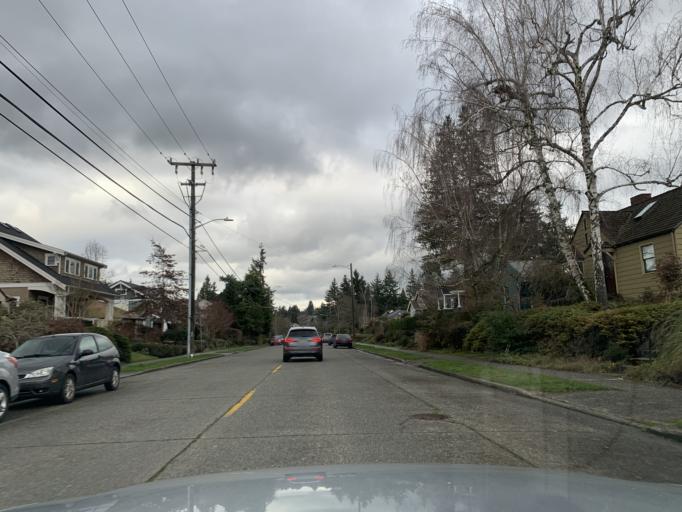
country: US
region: Washington
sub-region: King County
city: Yarrow Point
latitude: 47.6661
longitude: -122.2773
